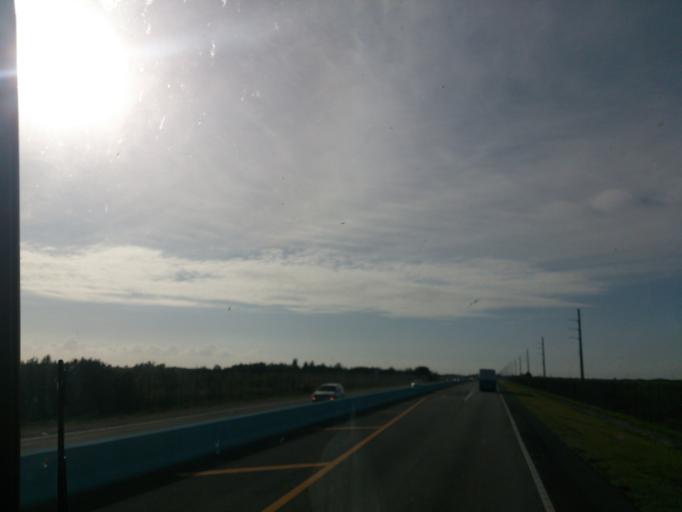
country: US
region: Florida
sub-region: Miami-Dade County
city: Florida City
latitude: 25.3855
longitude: -80.4656
